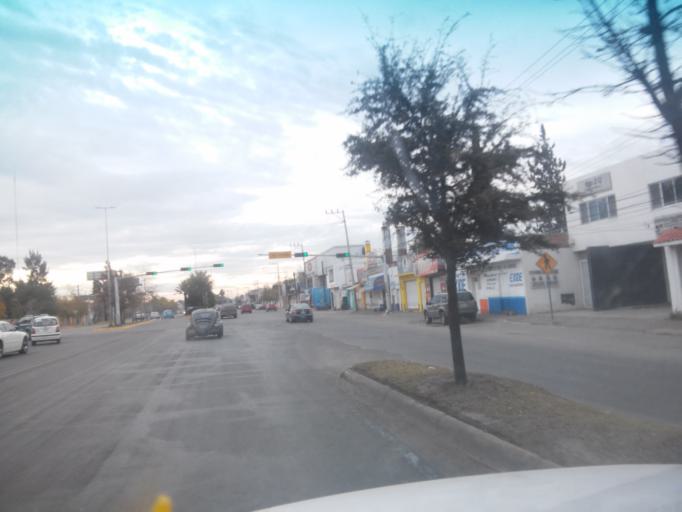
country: MX
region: Durango
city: Victoria de Durango
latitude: 24.0050
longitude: -104.6559
